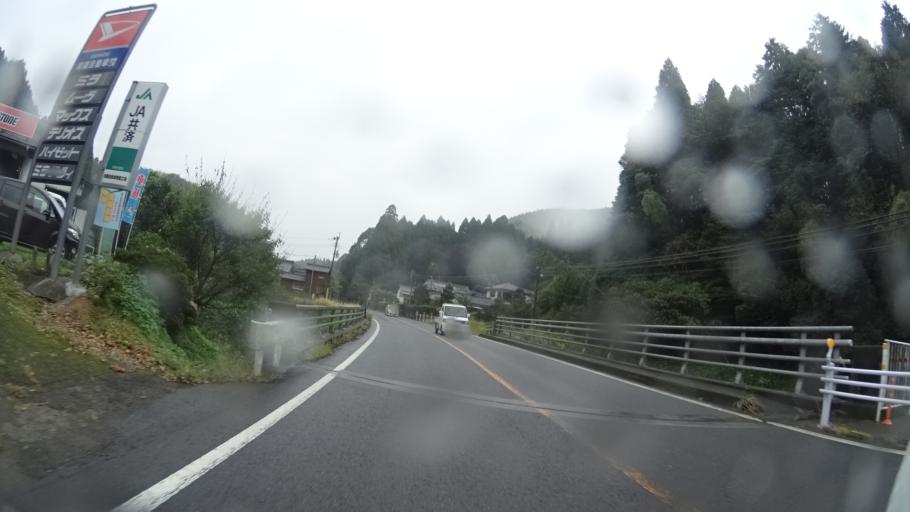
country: JP
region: Kagoshima
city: Kajiki
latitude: 31.8242
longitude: 130.6795
